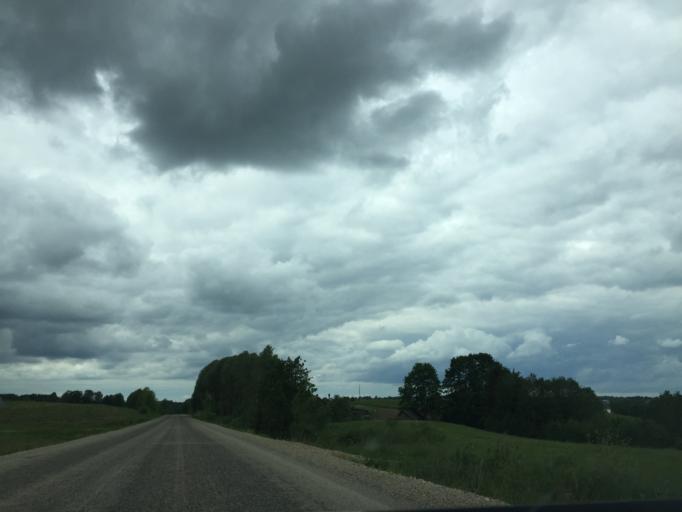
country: LV
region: Dagda
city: Dagda
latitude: 56.0755
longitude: 27.5442
